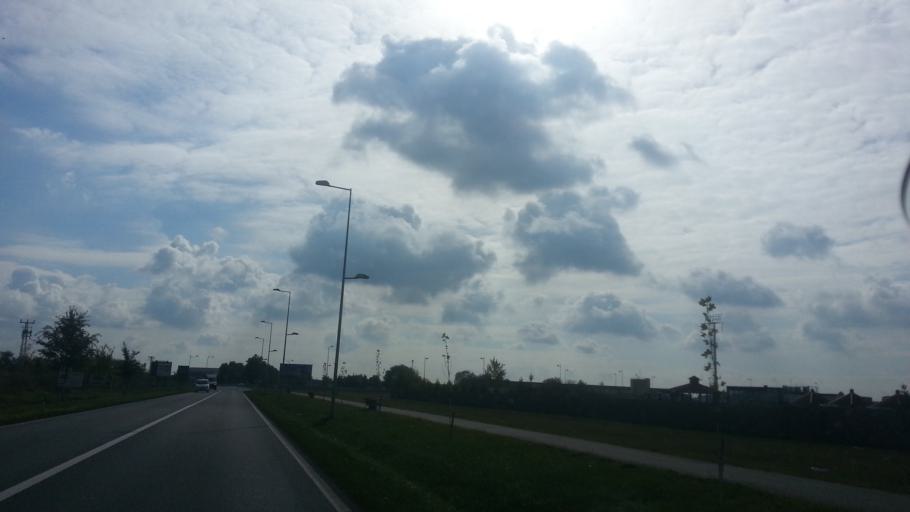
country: RS
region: Autonomna Pokrajina Vojvodina
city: Nova Pazova
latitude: 44.9585
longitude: 20.1978
